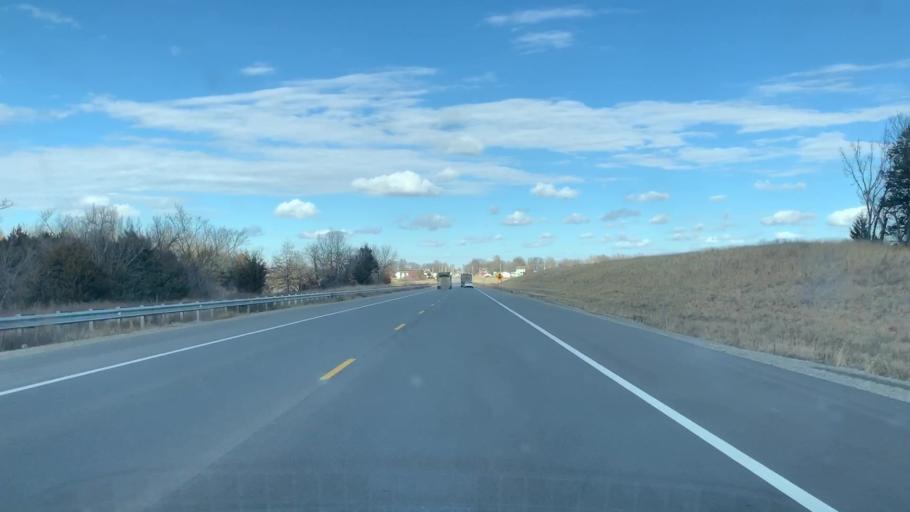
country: US
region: Kansas
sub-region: Crawford County
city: Pittsburg
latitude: 37.3336
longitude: -94.8321
